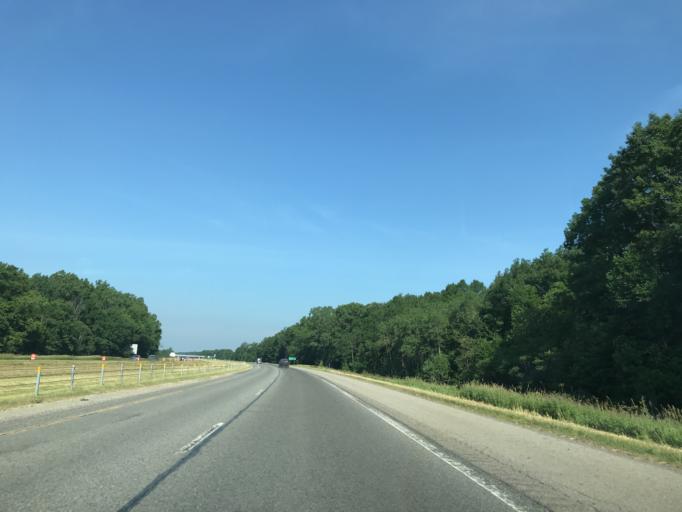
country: US
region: Michigan
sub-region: Ingham County
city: Webberville
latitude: 42.6656
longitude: -84.2130
